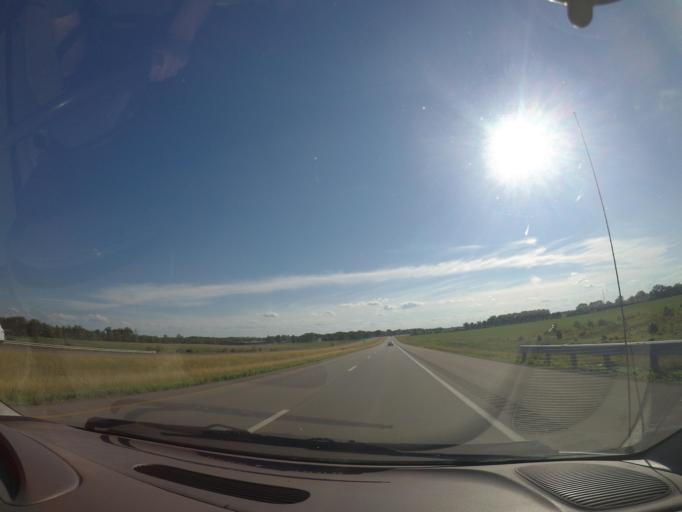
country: US
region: Ohio
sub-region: Henry County
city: Liberty Center
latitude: 41.4188
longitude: -84.0362
